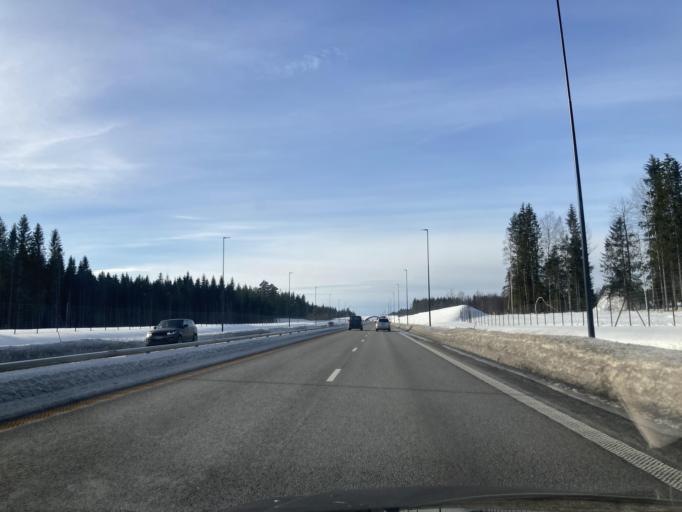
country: NO
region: Hedmark
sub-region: Loten
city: Loten
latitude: 60.8648
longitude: 11.4276
